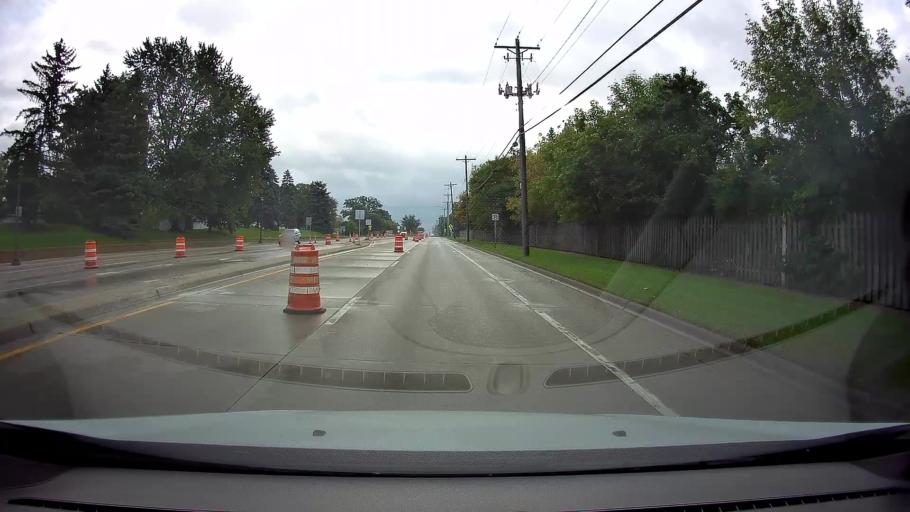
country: US
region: Minnesota
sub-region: Ramsey County
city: Lauderdale
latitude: 44.9916
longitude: -93.1994
